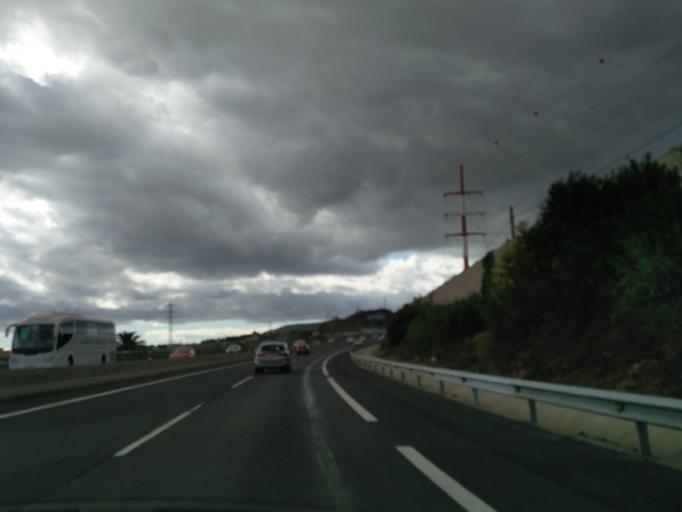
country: ES
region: Canary Islands
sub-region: Provincia de Santa Cruz de Tenerife
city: Las Rosas
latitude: 28.0496
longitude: -16.6280
